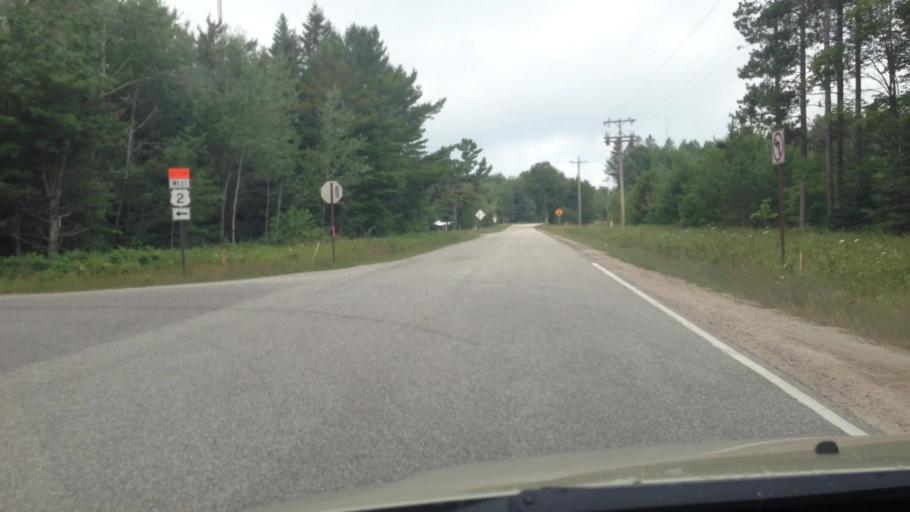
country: US
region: Michigan
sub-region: Mackinac County
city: Saint Ignace
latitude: 46.0569
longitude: -85.1505
